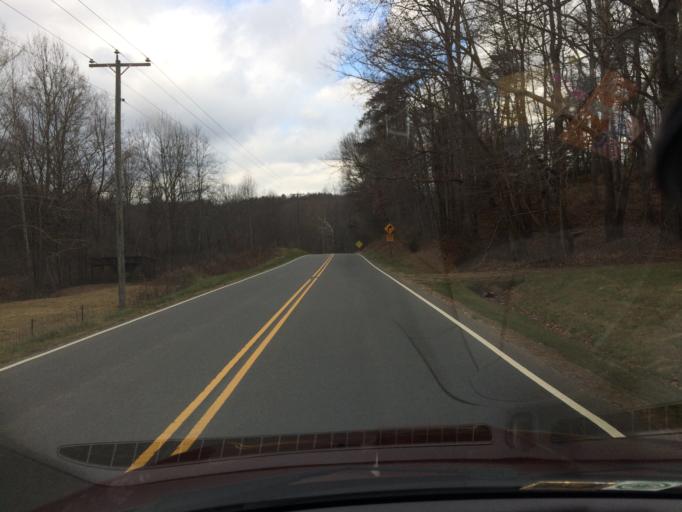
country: US
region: Virginia
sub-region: Patrick County
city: Stuart
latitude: 36.7494
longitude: -80.2664
